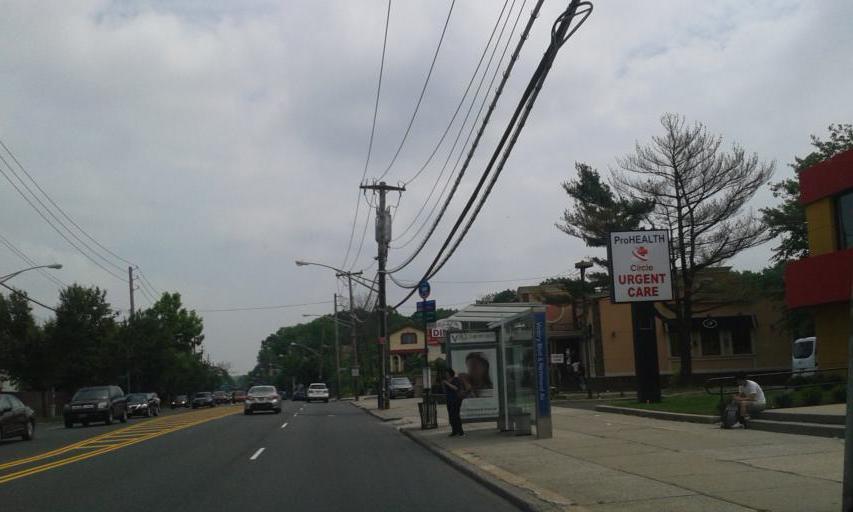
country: US
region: New York
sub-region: Richmond County
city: Bloomfield
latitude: 40.6072
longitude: -74.1615
